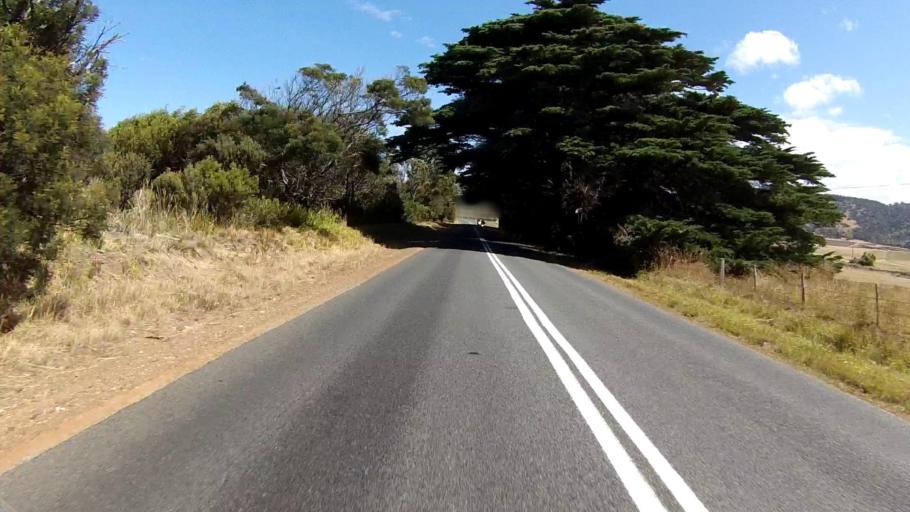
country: AU
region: Tasmania
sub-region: Sorell
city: Sorell
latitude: -42.1996
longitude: 148.0472
